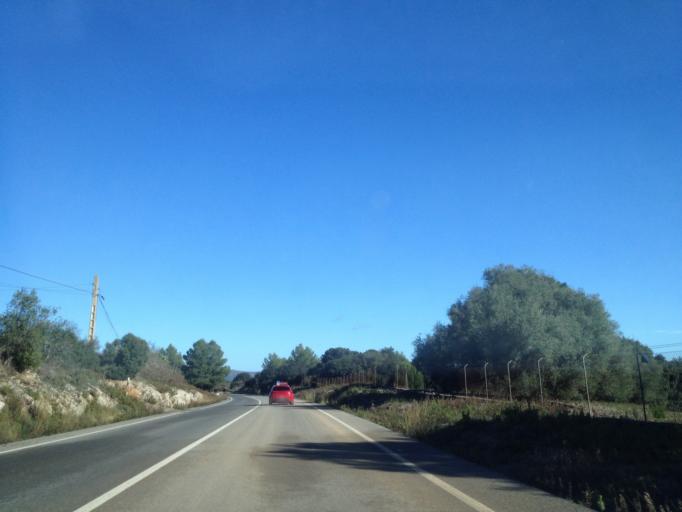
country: ES
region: Balearic Islands
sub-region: Illes Balears
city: Arta
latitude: 39.6654
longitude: 3.3214
